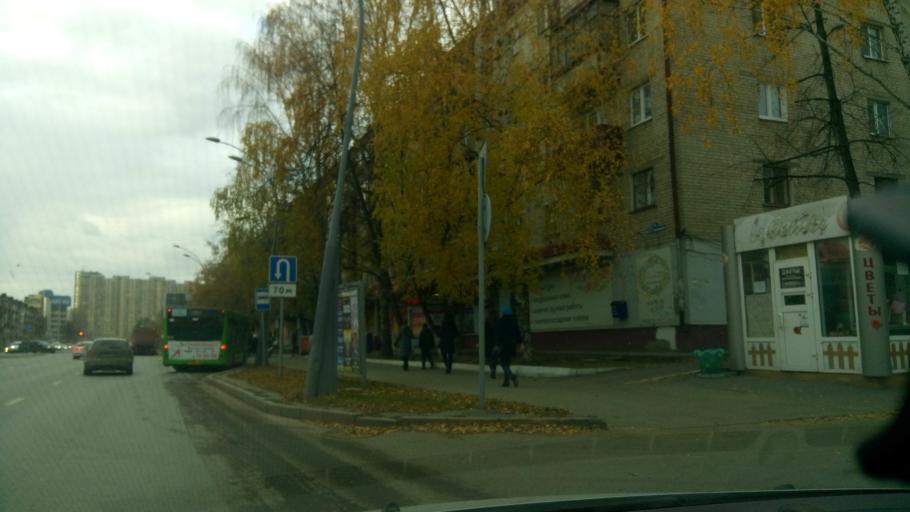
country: RU
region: Tjumen
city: Tyumen
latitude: 57.1410
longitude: 65.5742
